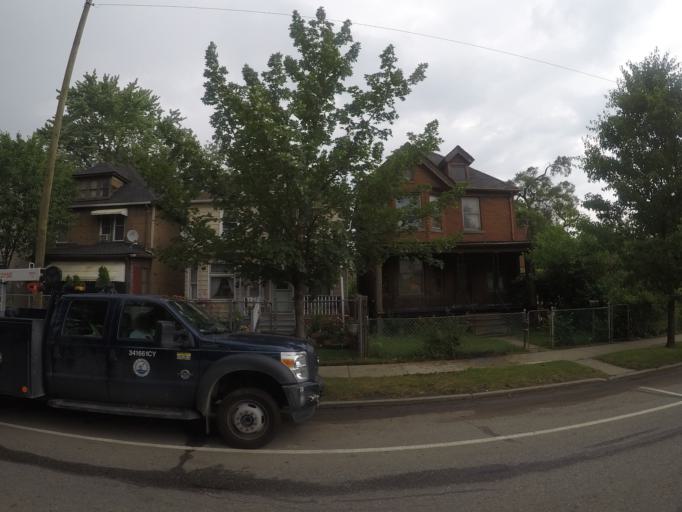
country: US
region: Michigan
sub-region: Wayne County
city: River Rouge
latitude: 42.3123
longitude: -83.1076
